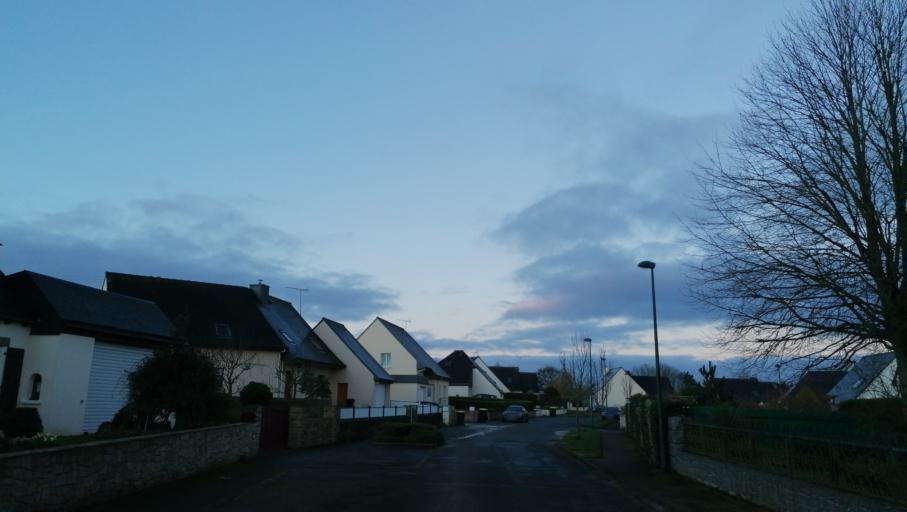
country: FR
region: Brittany
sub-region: Departement des Cotes-d'Armor
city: Plelo
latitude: 48.5527
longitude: -2.9494
